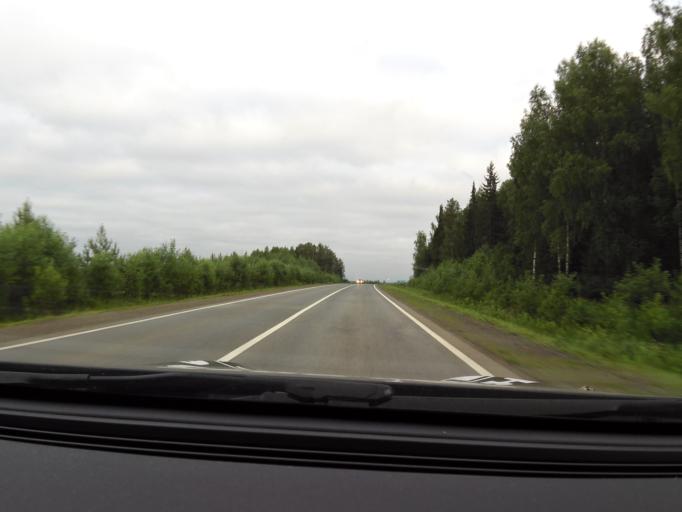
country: RU
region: Perm
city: Siva
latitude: 58.4274
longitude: 54.4499
